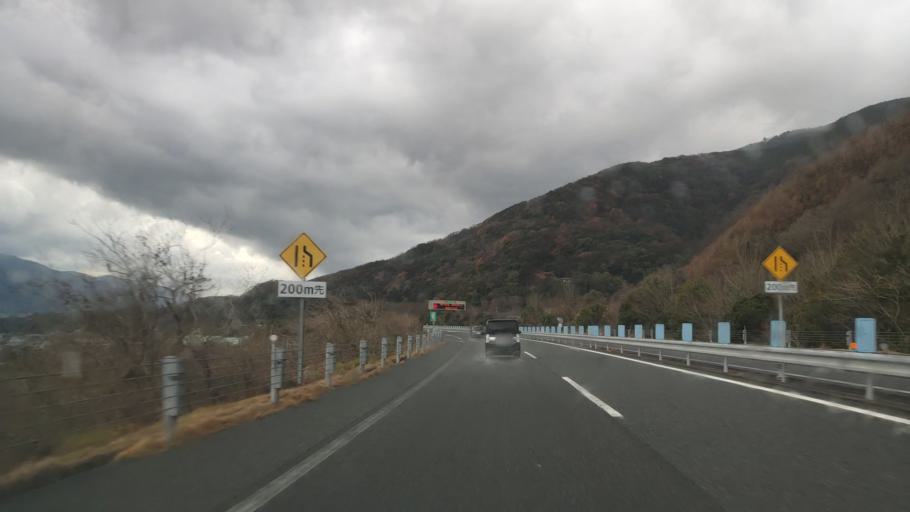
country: JP
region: Tokushima
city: Wakimachi
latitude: 34.0570
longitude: 133.9927
